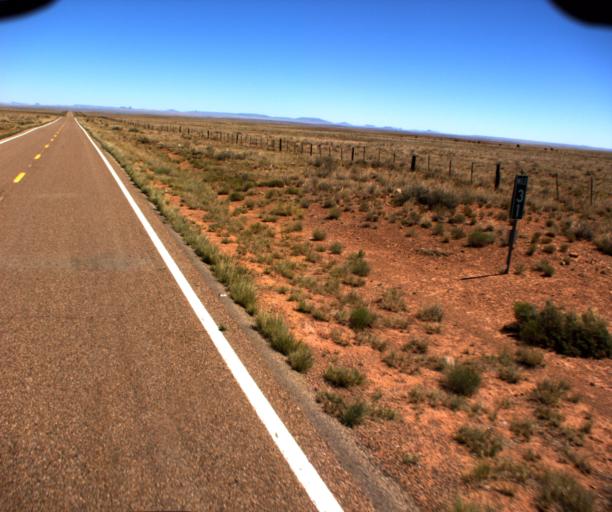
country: US
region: Arizona
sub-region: Navajo County
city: Winslow
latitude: 34.8690
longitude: -110.6574
